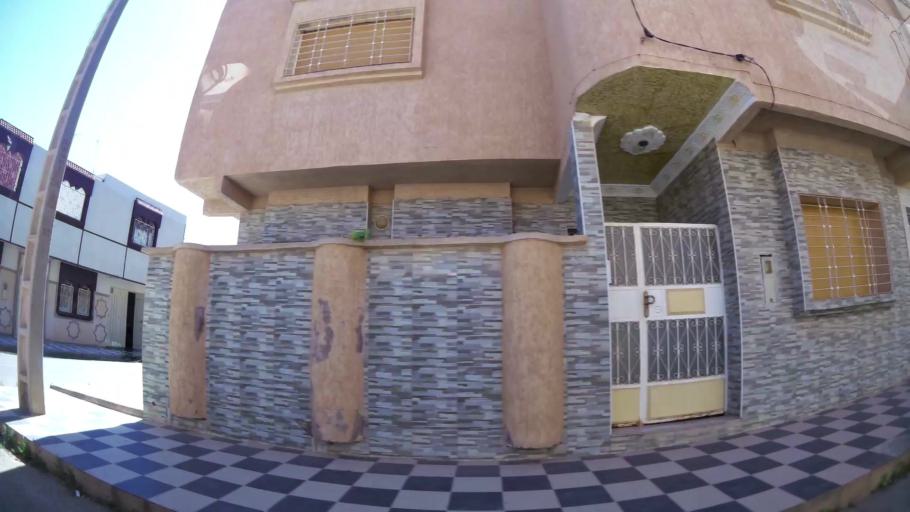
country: MA
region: Oriental
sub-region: Oujda-Angad
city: Oujda
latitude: 34.6590
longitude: -1.9309
